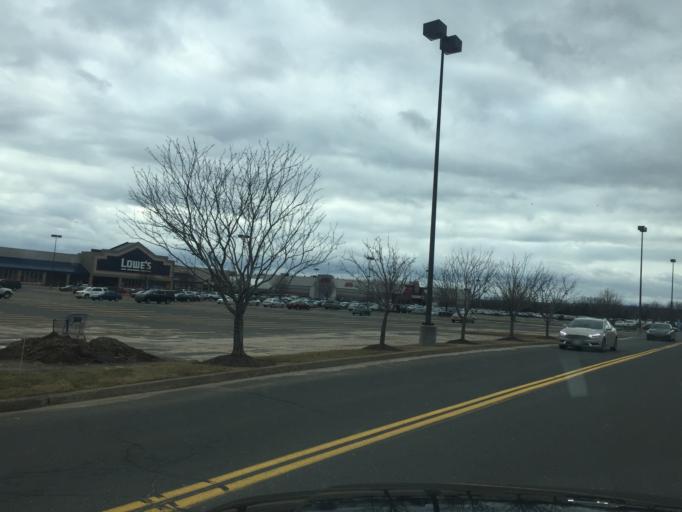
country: US
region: Connecticut
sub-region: Hartford County
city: Plainville
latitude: 41.6744
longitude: -72.8412
